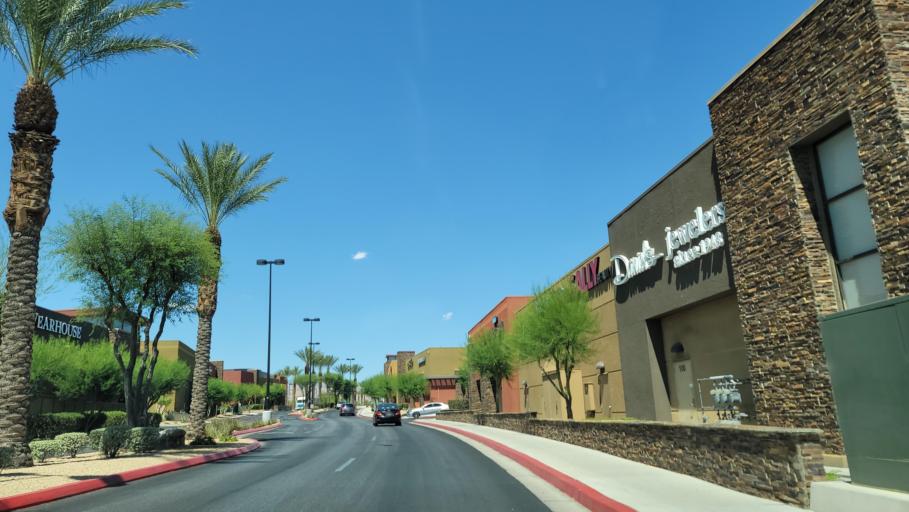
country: US
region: Nevada
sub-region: Clark County
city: Enterprise
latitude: 36.0633
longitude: -115.2504
